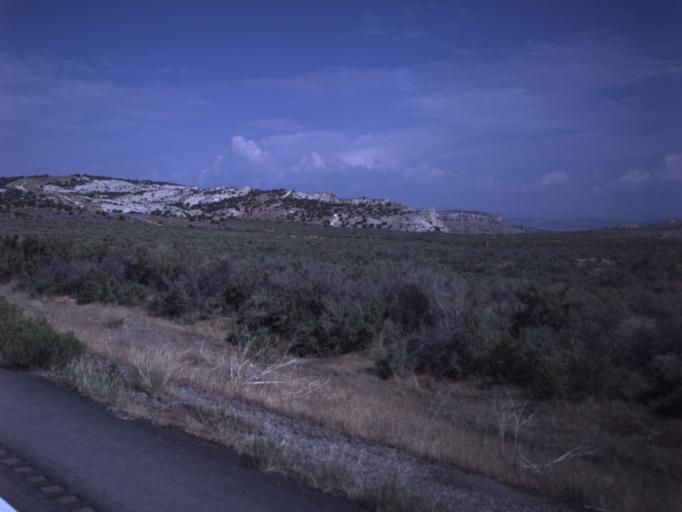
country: US
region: Utah
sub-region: Uintah County
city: Naples
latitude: 40.3174
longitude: -109.2386
